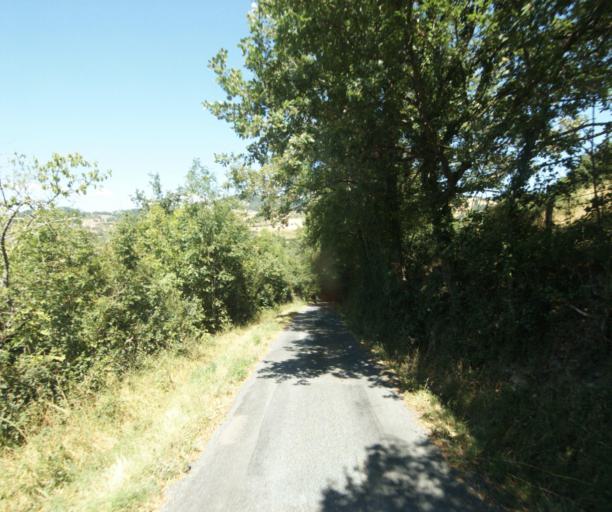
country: FR
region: Rhone-Alpes
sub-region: Departement du Rhone
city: Bessenay
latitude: 45.7934
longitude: 4.5288
